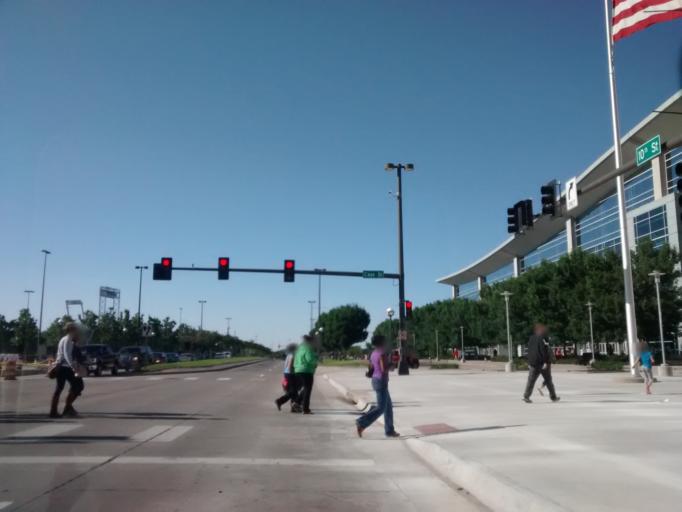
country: US
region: Nebraska
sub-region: Douglas County
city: Omaha
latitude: 41.2635
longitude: -95.9292
